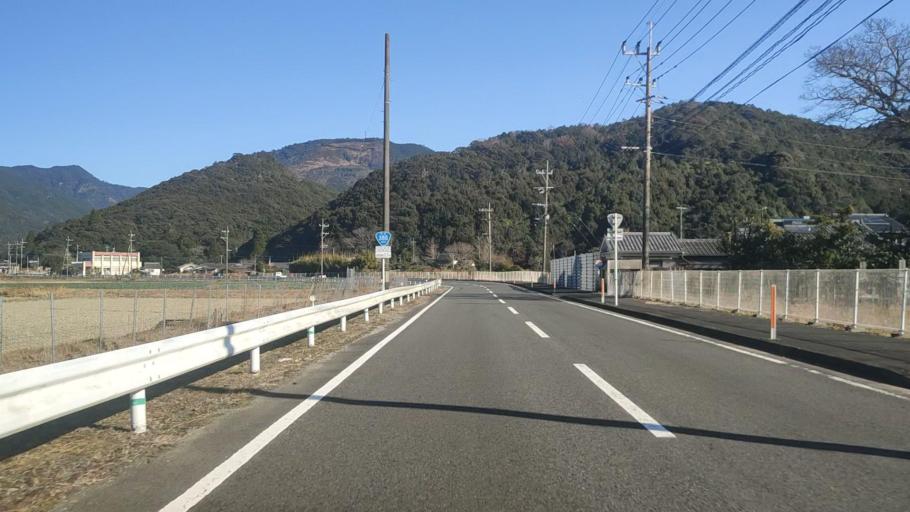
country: JP
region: Miyazaki
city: Nobeoka
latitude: 32.6807
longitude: 131.7868
